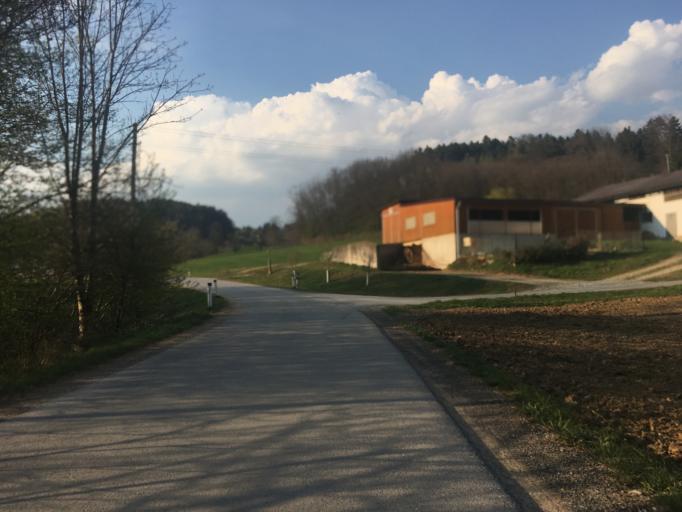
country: AT
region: Styria
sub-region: Politischer Bezirk Graz-Umgebung
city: Nestelbach bei Graz
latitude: 47.0819
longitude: 15.6264
